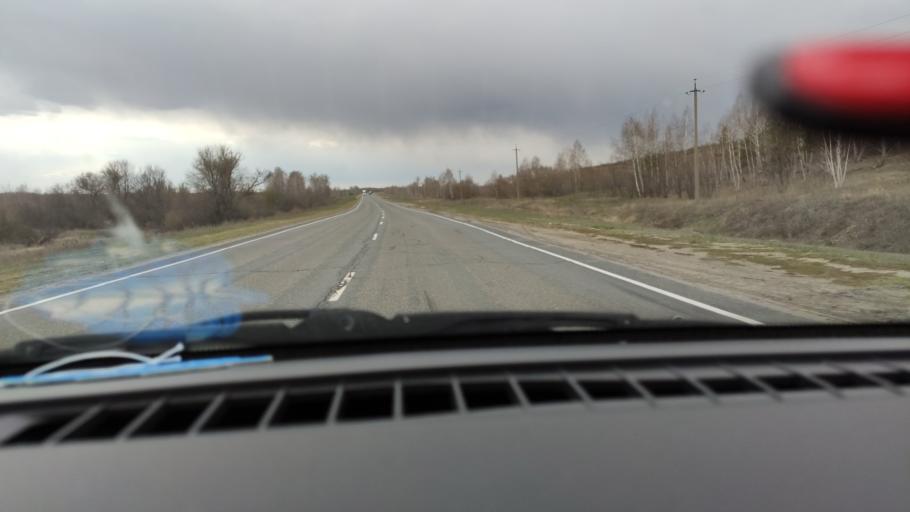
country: RU
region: Saratov
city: Sinodskoye
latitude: 52.0606
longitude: 46.7632
